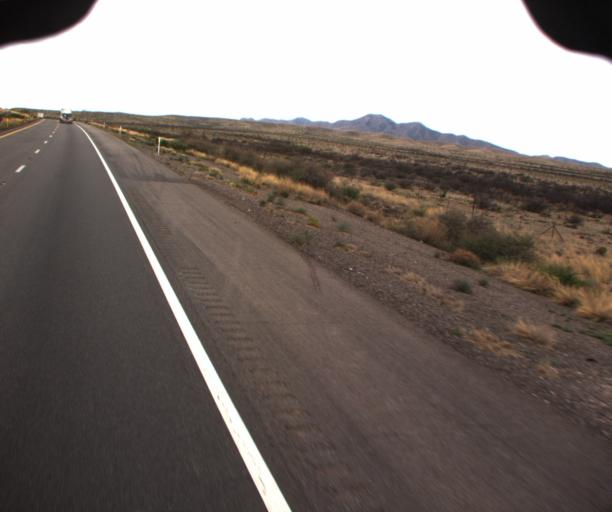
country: US
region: Arizona
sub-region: Cochise County
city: Willcox
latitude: 32.1481
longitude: -109.9954
